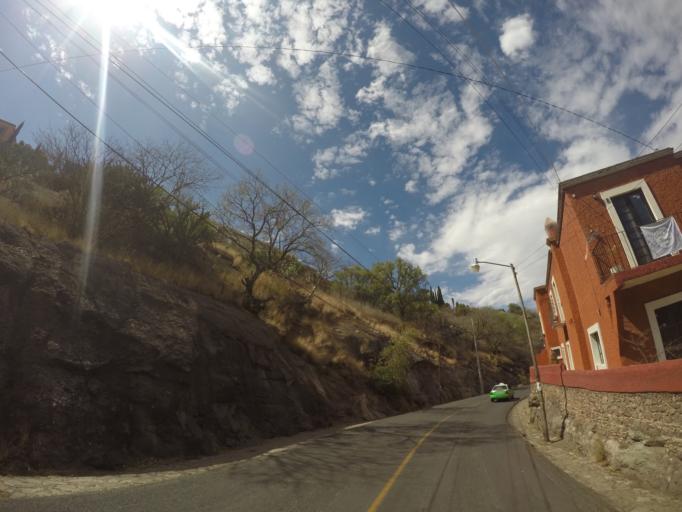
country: MX
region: Guanajuato
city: Guanajuato
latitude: 21.0124
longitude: -101.2551
